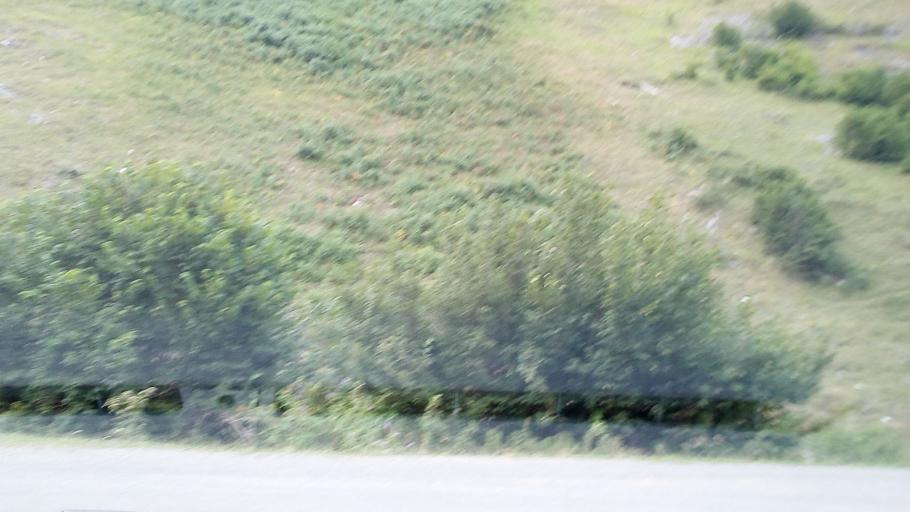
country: FR
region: Midi-Pyrenees
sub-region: Departement des Hautes-Pyrenees
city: Cauterets
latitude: 42.9100
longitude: -0.2019
